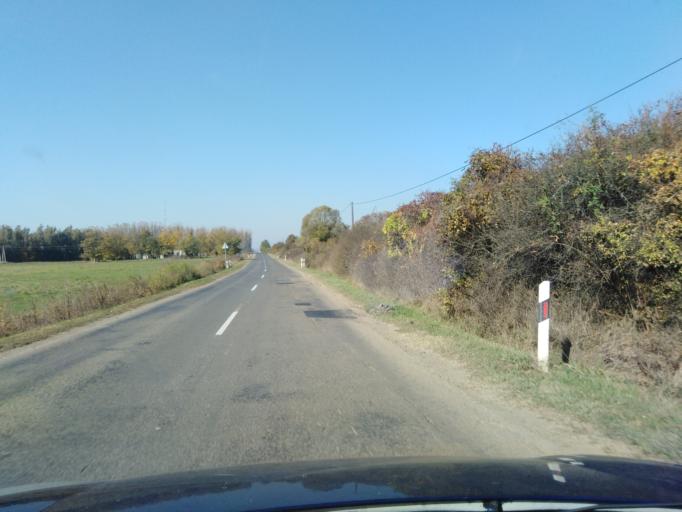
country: HU
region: Nograd
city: Karancslapujto
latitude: 48.1530
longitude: 19.7168
